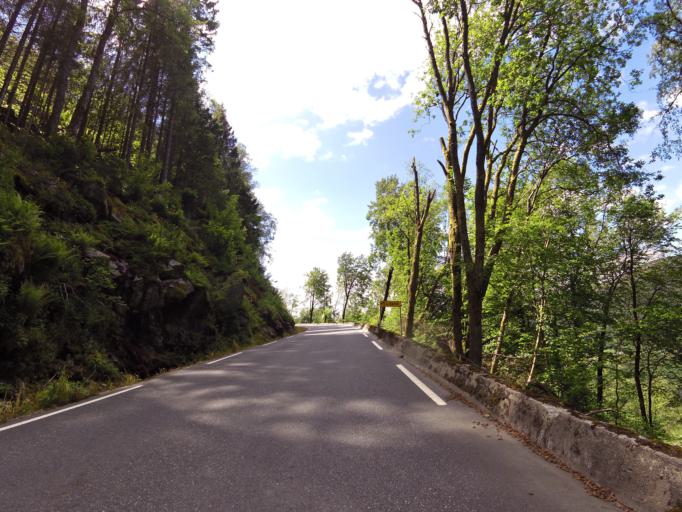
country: NO
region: Vest-Agder
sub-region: Kvinesdal
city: Liknes
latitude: 58.2929
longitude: 6.9429
